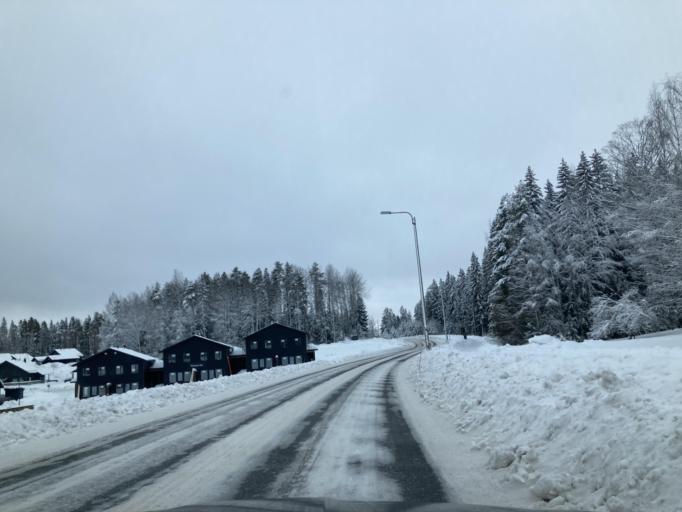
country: FI
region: Central Finland
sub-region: Jaemsae
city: Jaemsae
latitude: 61.8771
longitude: 25.2786
